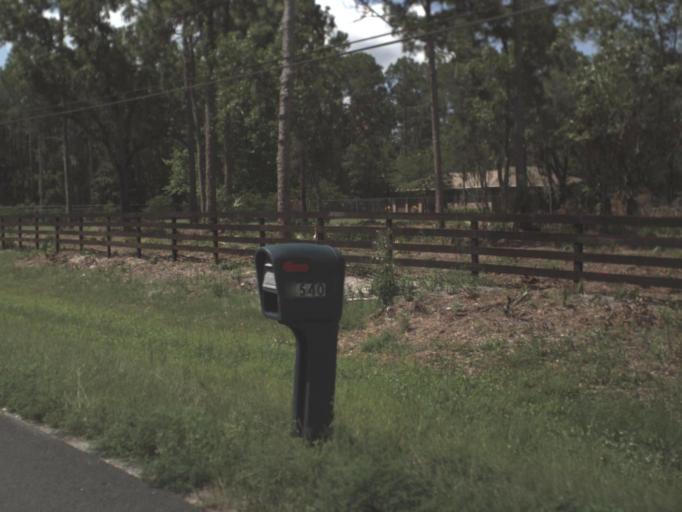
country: US
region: Florida
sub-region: Clay County
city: Green Cove Springs
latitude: 29.9728
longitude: -81.5397
